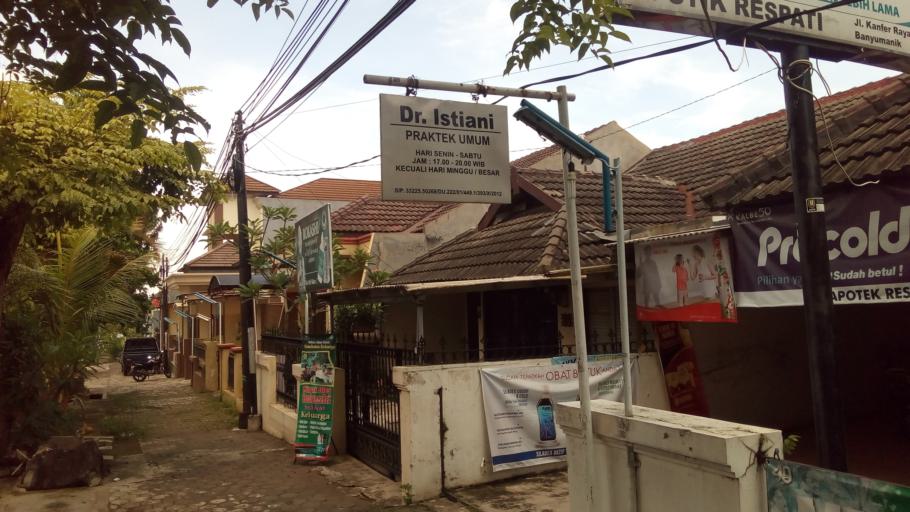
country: ID
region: Central Java
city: Ungaran
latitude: -7.0713
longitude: 110.4271
